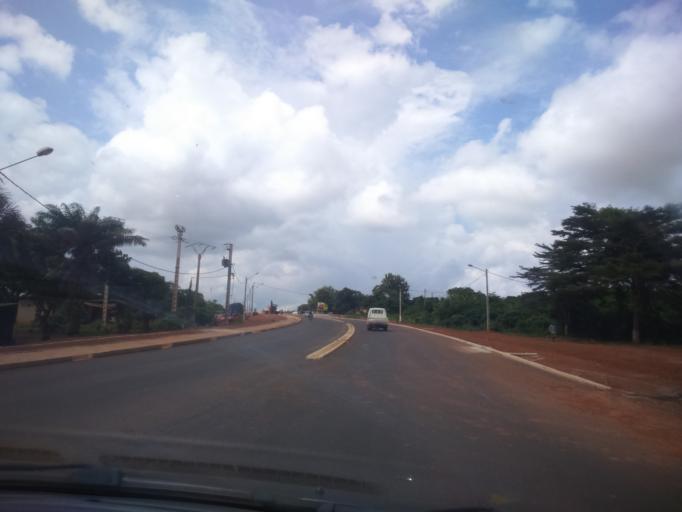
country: CI
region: Moyen-Comoe
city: Abengourou
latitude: 6.7184
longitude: -3.5187
